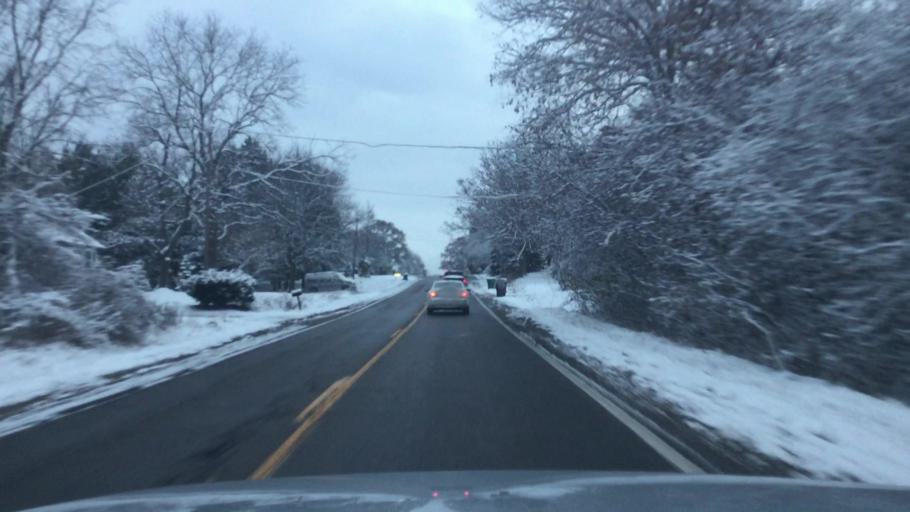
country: US
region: Michigan
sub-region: Oakland County
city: West Bloomfield Township
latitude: 42.6208
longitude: -83.3990
